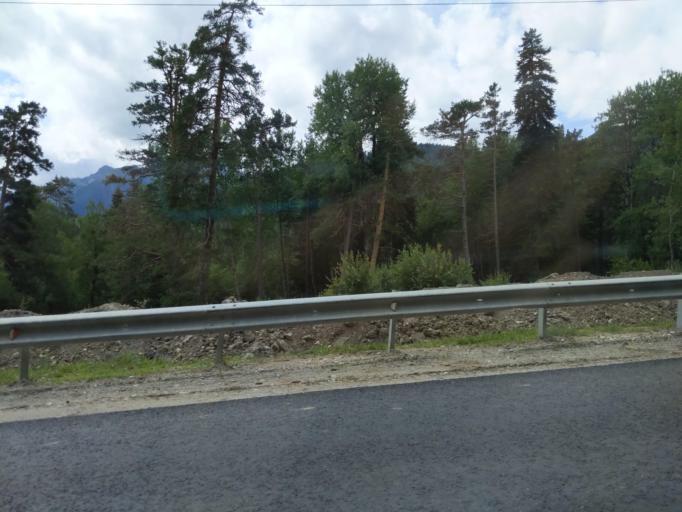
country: RU
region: Karachayevo-Cherkesiya
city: Nizhniy Arkhyz
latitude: 43.5372
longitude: 41.2134
